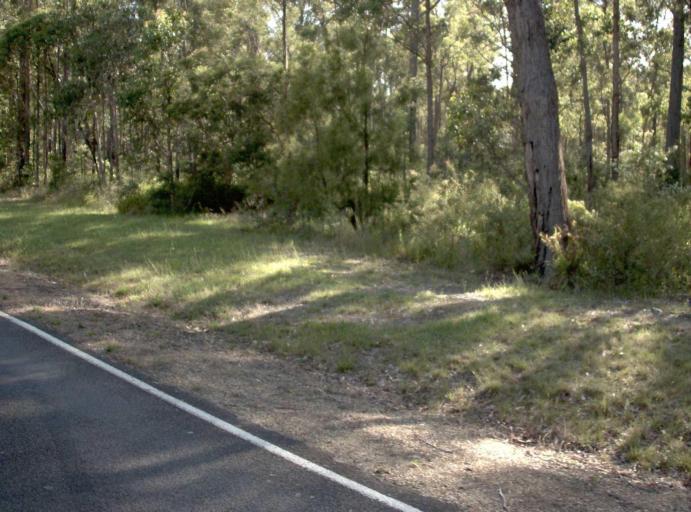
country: AU
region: Victoria
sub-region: East Gippsland
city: Lakes Entrance
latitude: -37.6844
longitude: 148.4699
